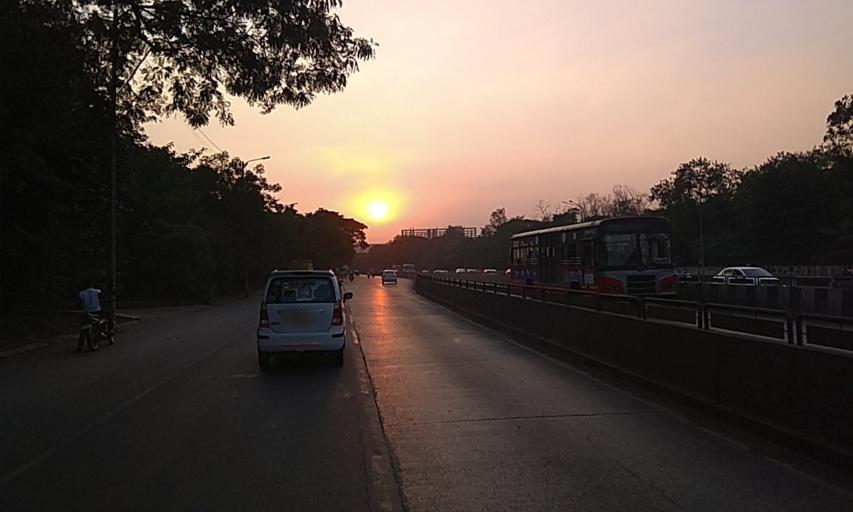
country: IN
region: Maharashtra
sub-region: Pune Division
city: Lohogaon
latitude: 18.5545
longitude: 73.9040
